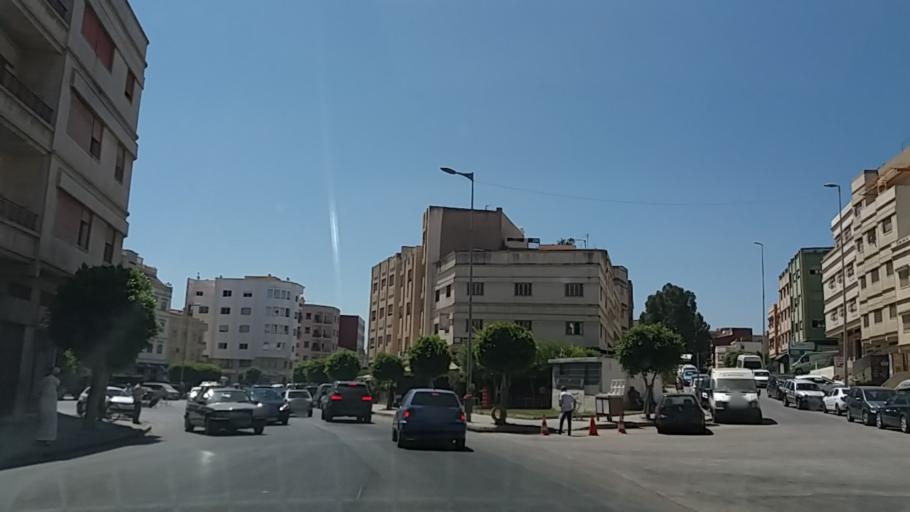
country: MA
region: Tanger-Tetouan
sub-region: Tanger-Assilah
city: Tangier
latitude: 35.7562
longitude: -5.8014
